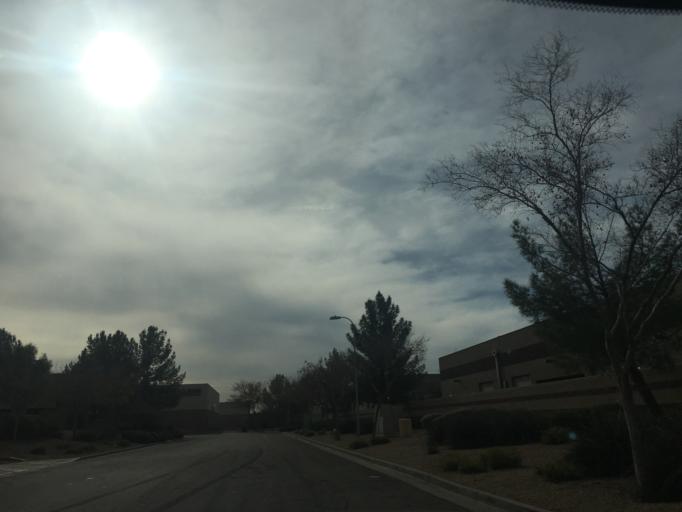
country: US
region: Arizona
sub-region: Maricopa County
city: San Carlos
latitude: 33.3667
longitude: -111.8235
